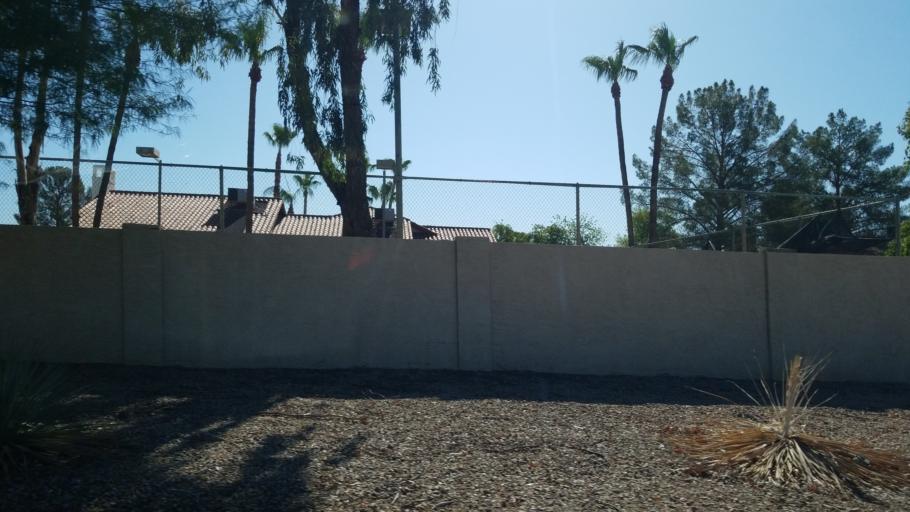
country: US
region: Arizona
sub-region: Maricopa County
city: Peoria
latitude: 33.6005
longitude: -112.2026
